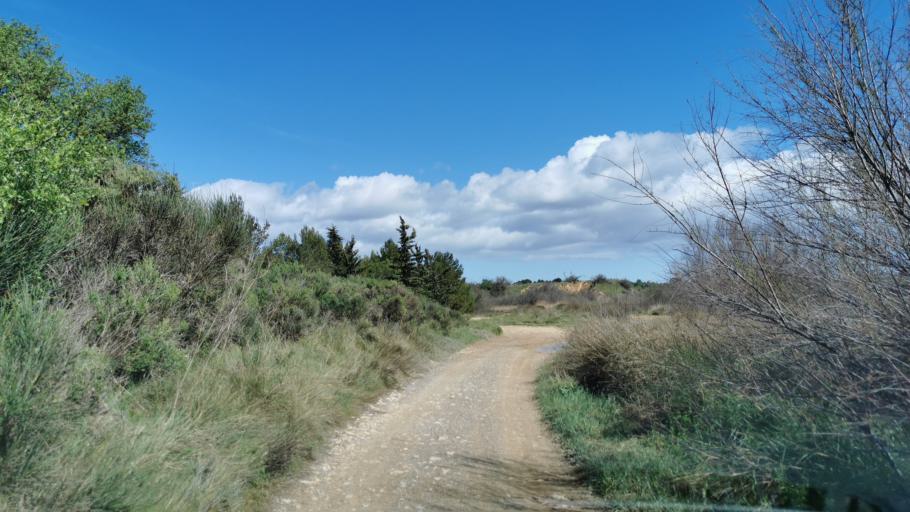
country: FR
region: Languedoc-Roussillon
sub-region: Departement de l'Aude
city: Narbonne
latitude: 43.1488
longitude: 2.9864
